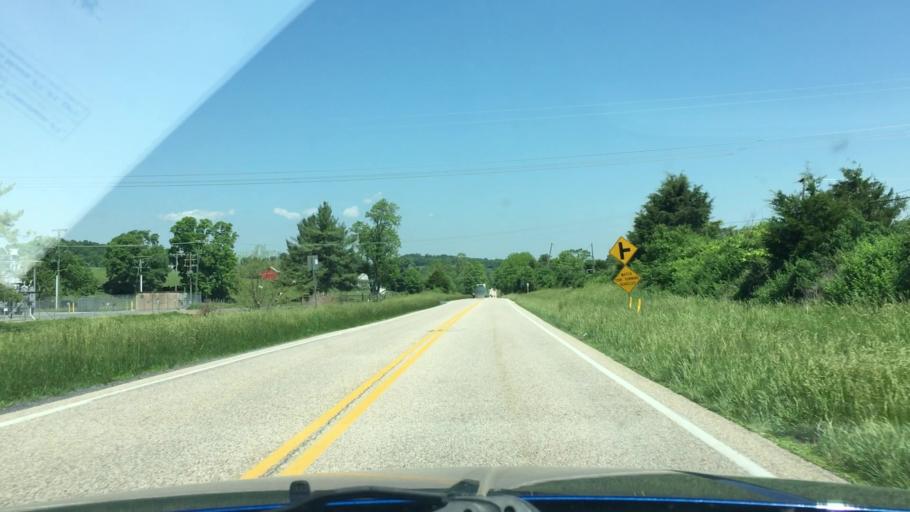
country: US
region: Virginia
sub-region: City of Staunton
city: Staunton
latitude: 38.1932
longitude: -79.1126
